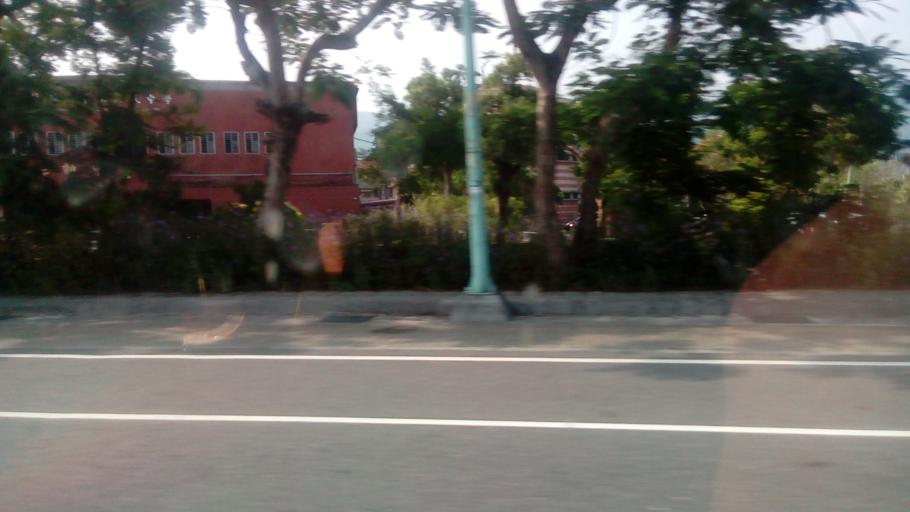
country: TW
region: Taiwan
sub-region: Yilan
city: Yilan
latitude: 24.6328
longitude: 121.7920
